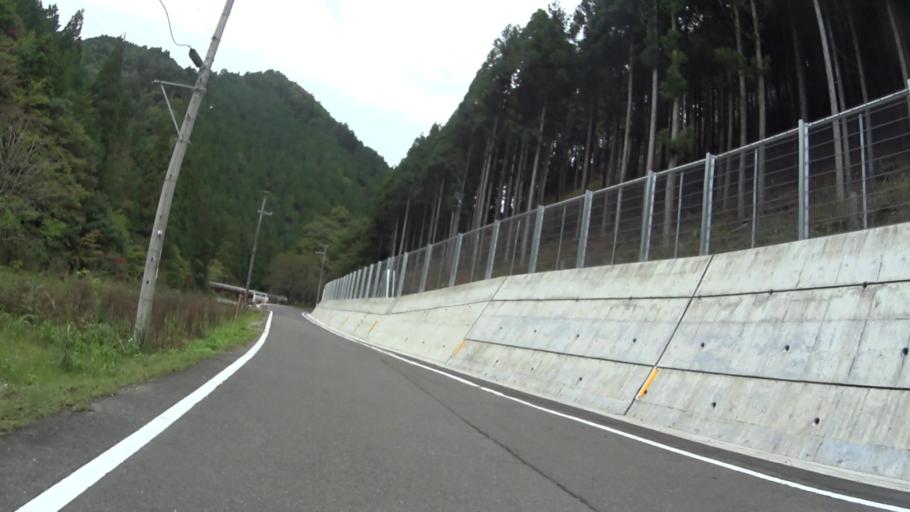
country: JP
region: Fukui
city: Obama
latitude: 35.2887
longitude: 135.6953
